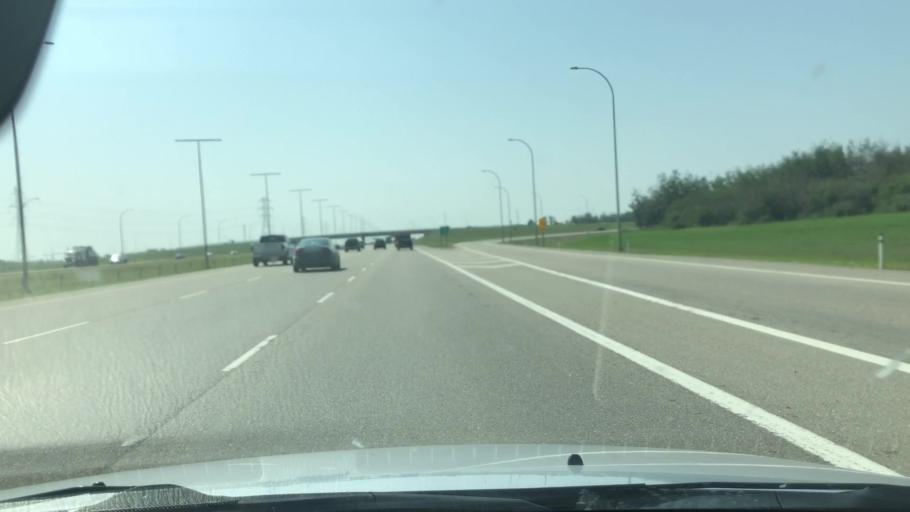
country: CA
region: Alberta
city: St. Albert
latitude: 53.5285
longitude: -113.6596
